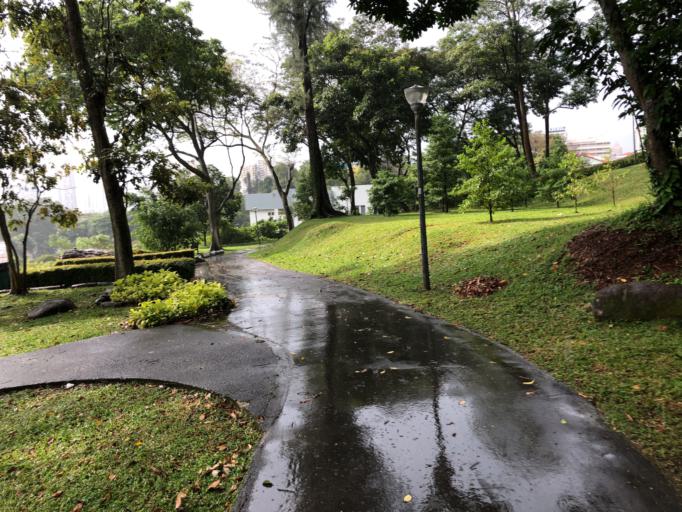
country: SG
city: Singapore
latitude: 1.2843
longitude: 103.8389
